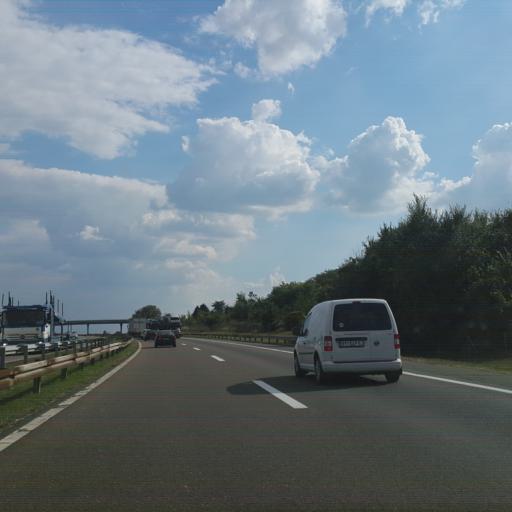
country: RS
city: Lugavcina
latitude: 44.4468
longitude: 21.0461
